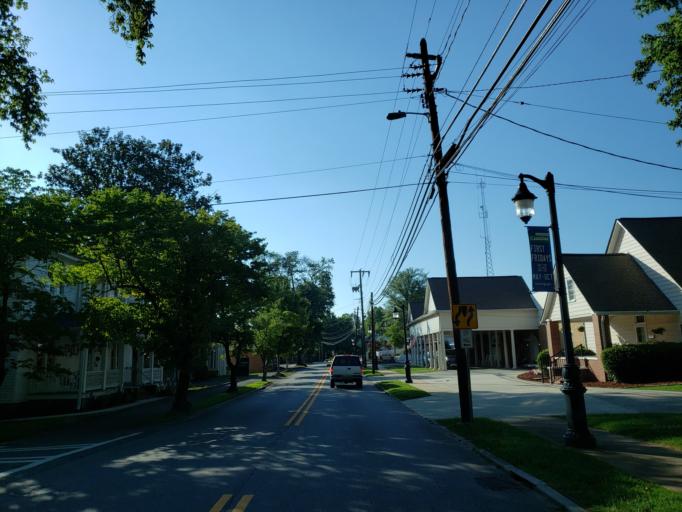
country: US
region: Georgia
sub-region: Cherokee County
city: Canton
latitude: 34.2354
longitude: -84.4865
